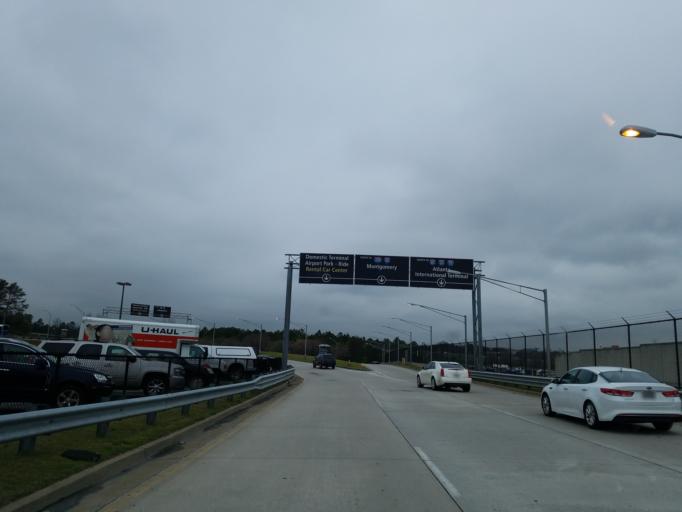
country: US
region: Georgia
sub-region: Fulton County
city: College Park
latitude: 33.6455
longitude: -84.4435
